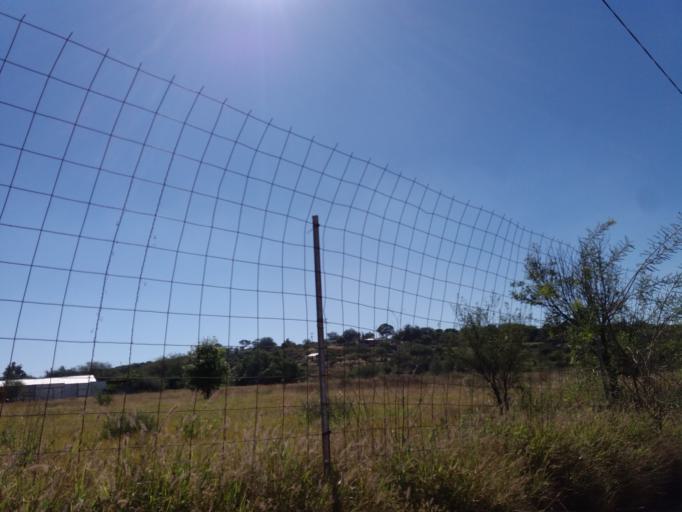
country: MX
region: Aguascalientes
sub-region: Aguascalientes
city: Villa Licenciado Jesus Teran (Calvillito)
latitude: 21.8599
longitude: -102.2301
